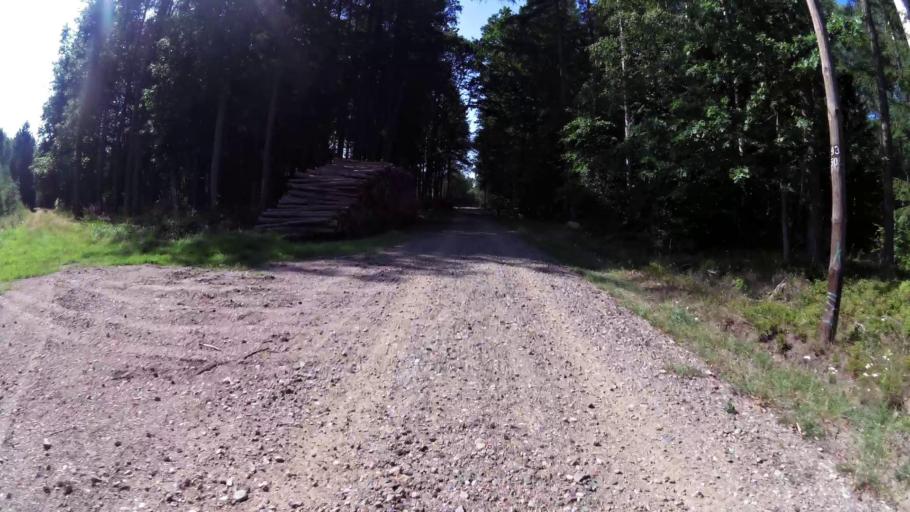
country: PL
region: West Pomeranian Voivodeship
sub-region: Powiat drawski
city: Czaplinek
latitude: 53.4016
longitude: 16.2468
